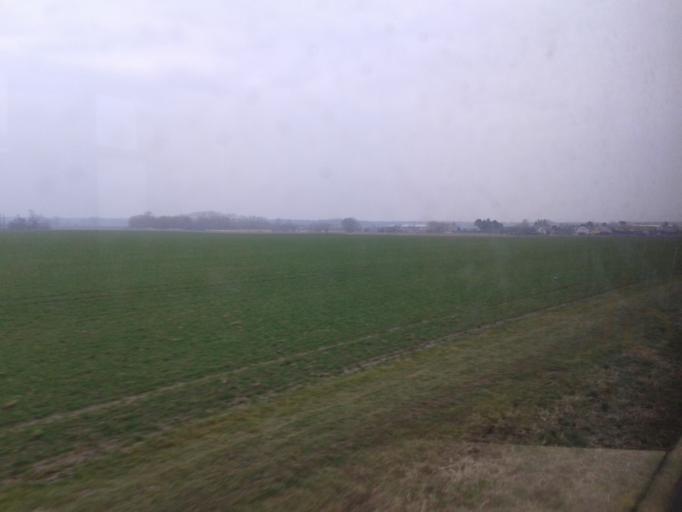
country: CZ
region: Olomoucky
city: Skrben
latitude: 49.6394
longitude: 17.1627
